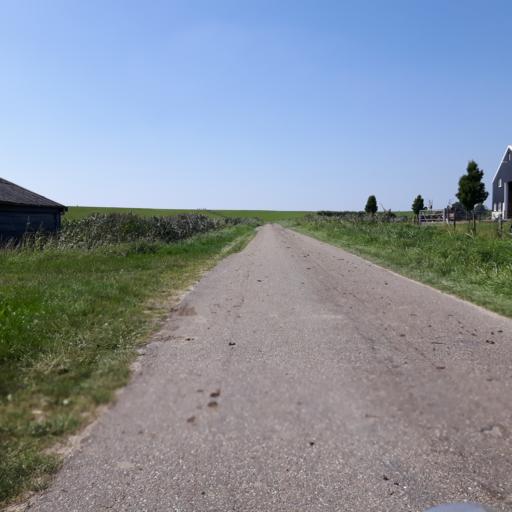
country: NL
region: Zeeland
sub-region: Gemeente Reimerswaal
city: Yerseke
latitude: 51.4161
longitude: 4.0627
